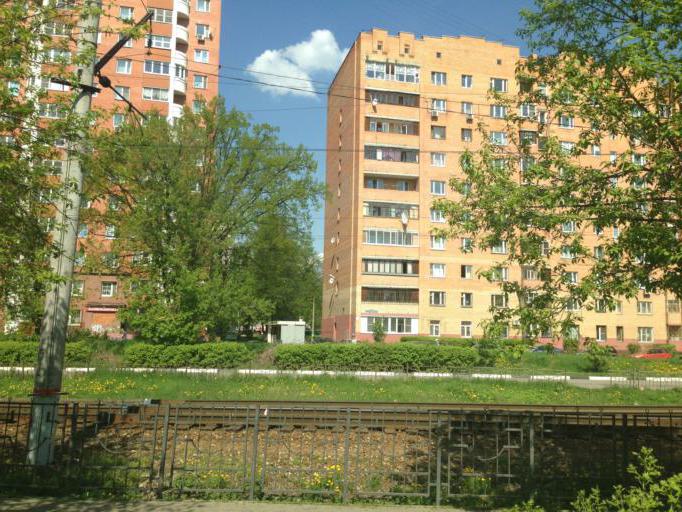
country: RU
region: Moskovskaya
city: Balashikha
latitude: 55.8082
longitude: 37.9464
